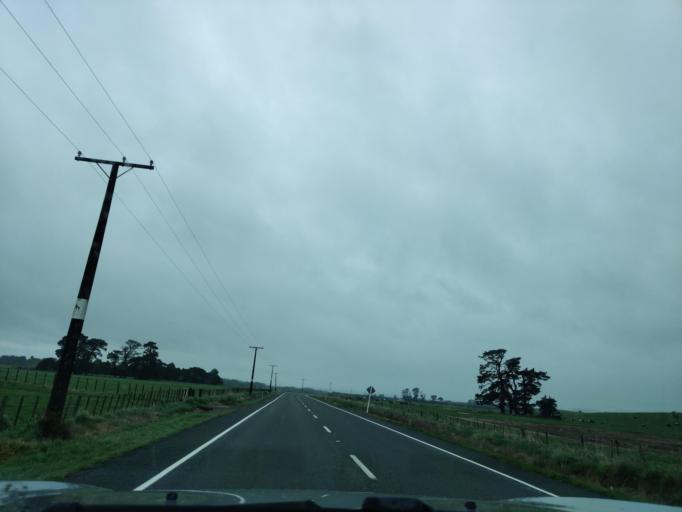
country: NZ
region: Hawke's Bay
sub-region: Hastings District
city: Hastings
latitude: -40.0202
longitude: 176.2725
